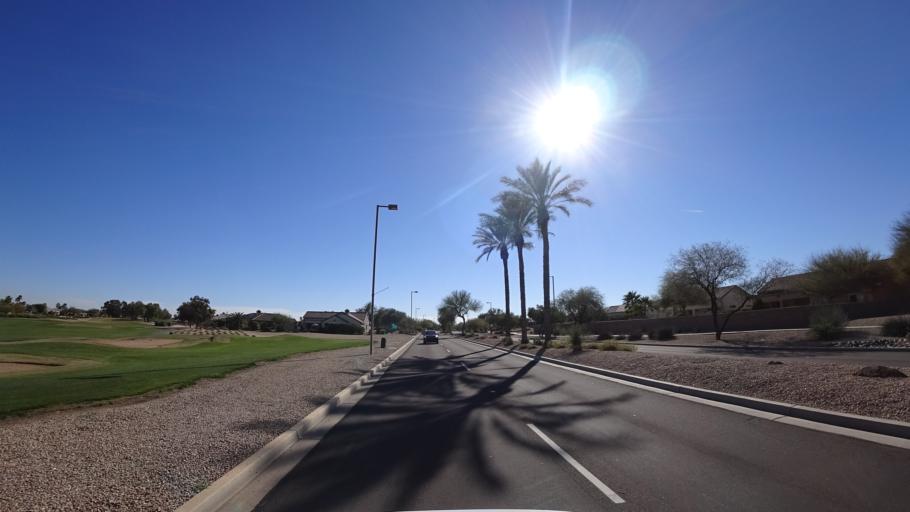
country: US
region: Arizona
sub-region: Maricopa County
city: Sun City West
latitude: 33.6507
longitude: -112.4056
